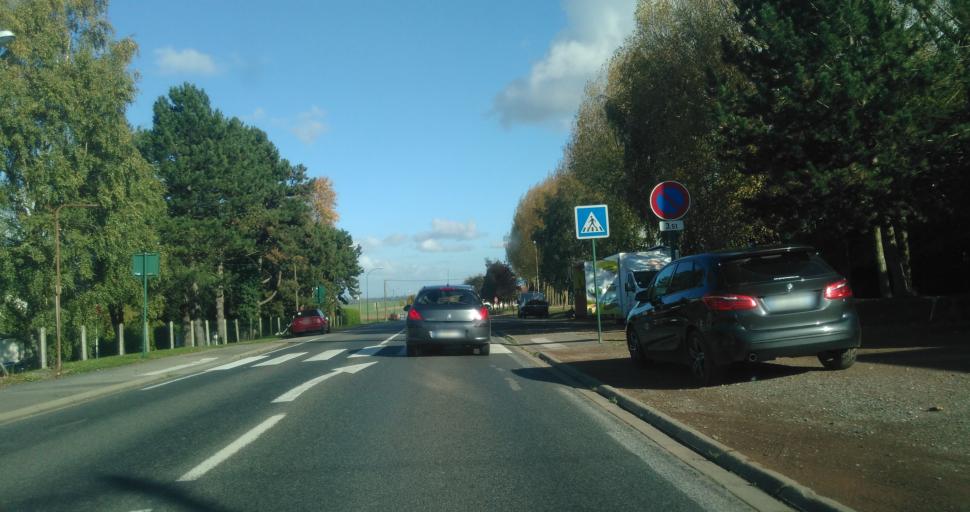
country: FR
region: Nord-Pas-de-Calais
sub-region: Departement du Pas-de-Calais
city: Beaumetz-les-Loges
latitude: 50.2437
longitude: 2.6634
